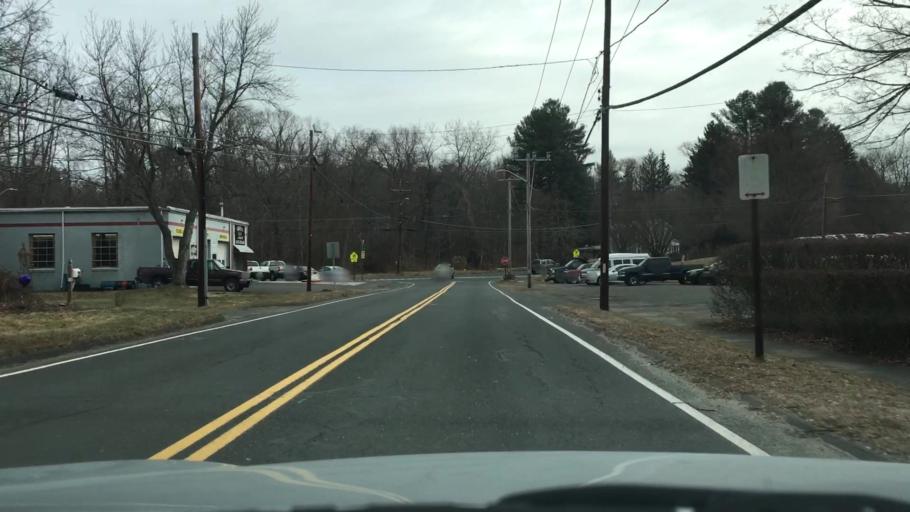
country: US
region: Massachusetts
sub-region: Hampshire County
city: Northampton
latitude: 42.3261
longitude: -72.6536
